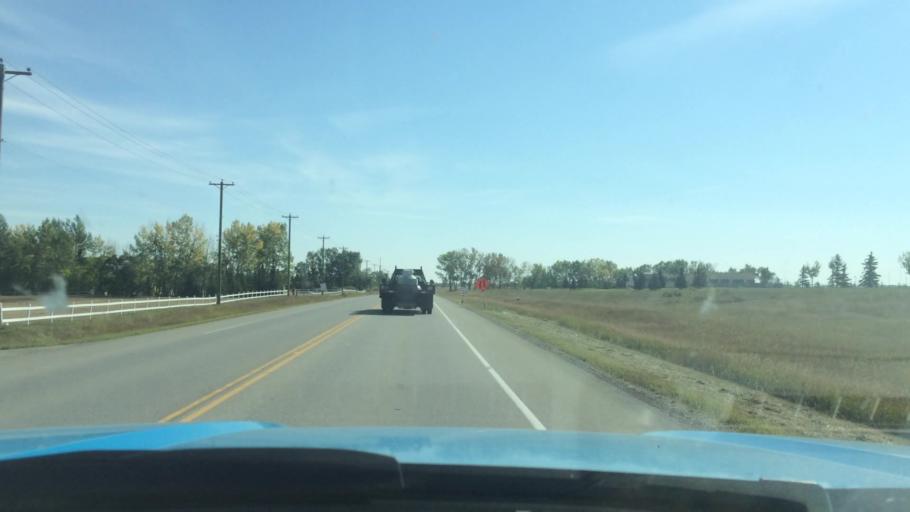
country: CA
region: Alberta
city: Airdrie
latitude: 51.2124
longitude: -113.9681
